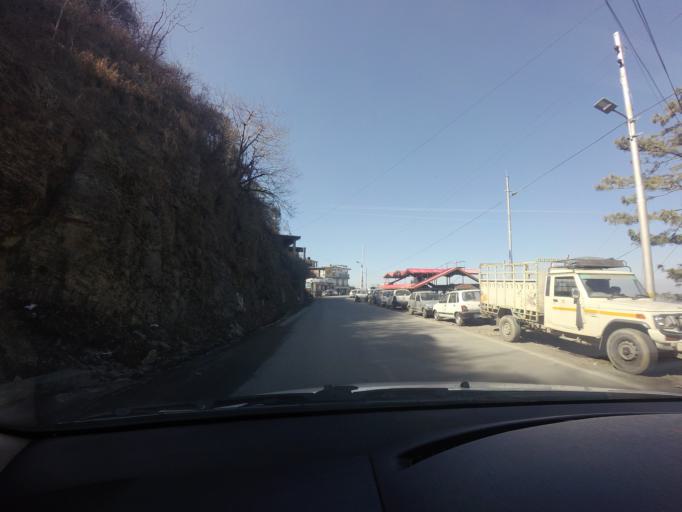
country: IN
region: Himachal Pradesh
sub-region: Shimla
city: Shimla
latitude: 31.1082
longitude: 77.2112
